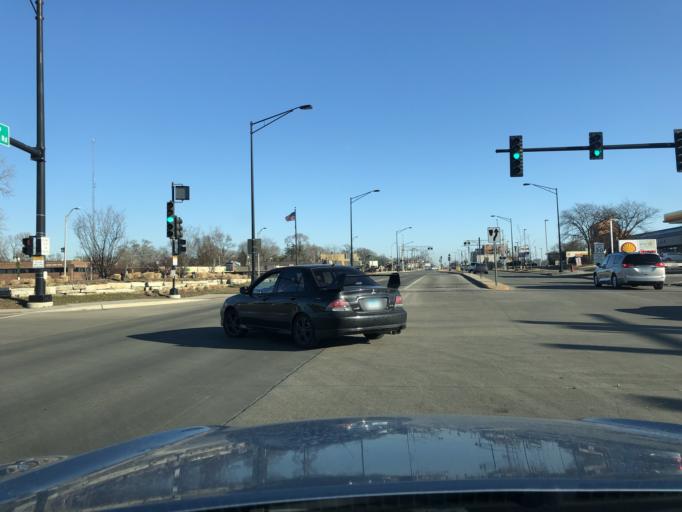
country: US
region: Illinois
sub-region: DuPage County
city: Wood Dale
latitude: 41.9633
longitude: -87.9789
